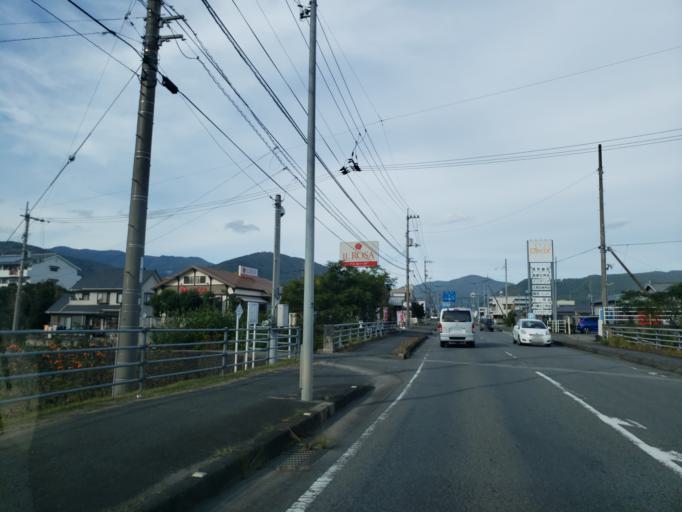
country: JP
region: Tokushima
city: Wakimachi
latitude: 34.0632
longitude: 134.1693
